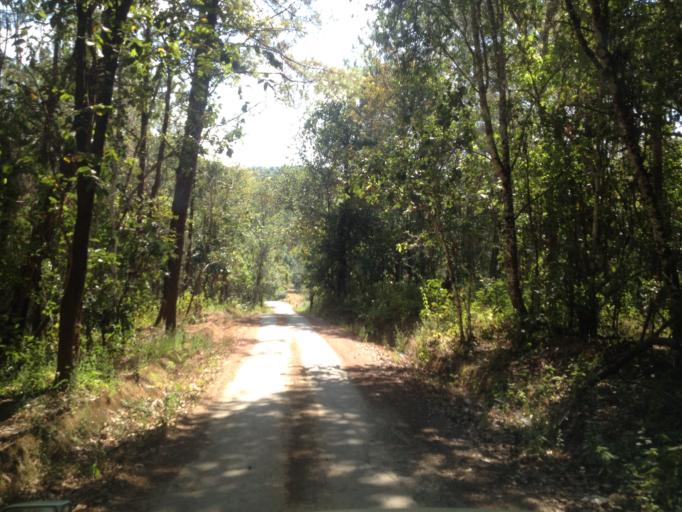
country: TH
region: Mae Hong Son
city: Ban Huai I Huak
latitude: 18.1070
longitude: 98.1718
